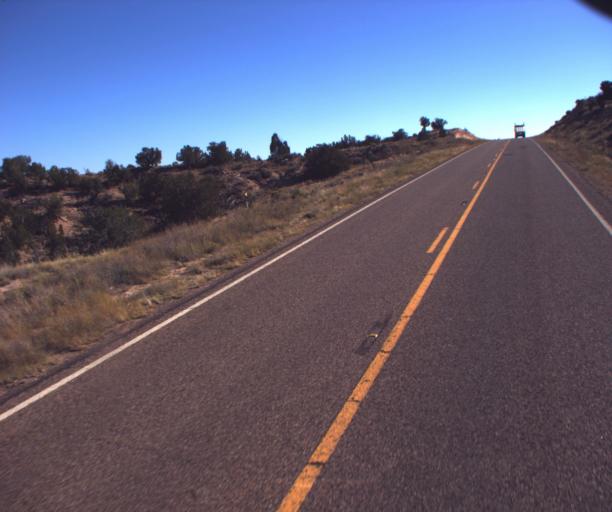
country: US
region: Arizona
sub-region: Apache County
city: Ganado
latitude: 35.4743
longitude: -109.5297
